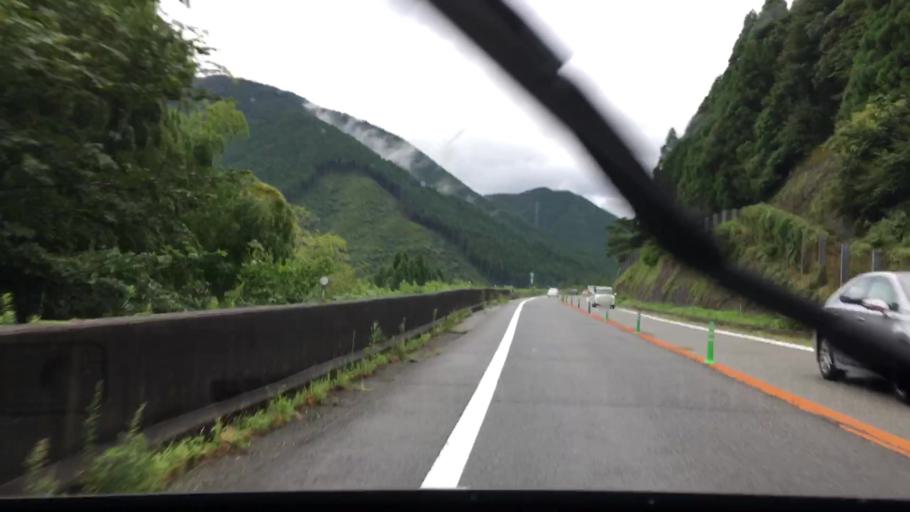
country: JP
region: Hyogo
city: Nishiwaki
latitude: 35.1319
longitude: 134.7876
